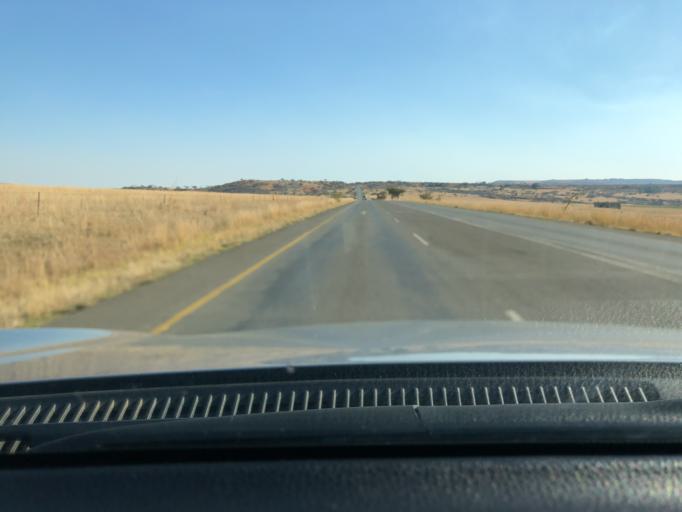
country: ZA
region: KwaZulu-Natal
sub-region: uMzinyathi District Municipality
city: Glencoe
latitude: -28.2926
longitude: 30.0756
